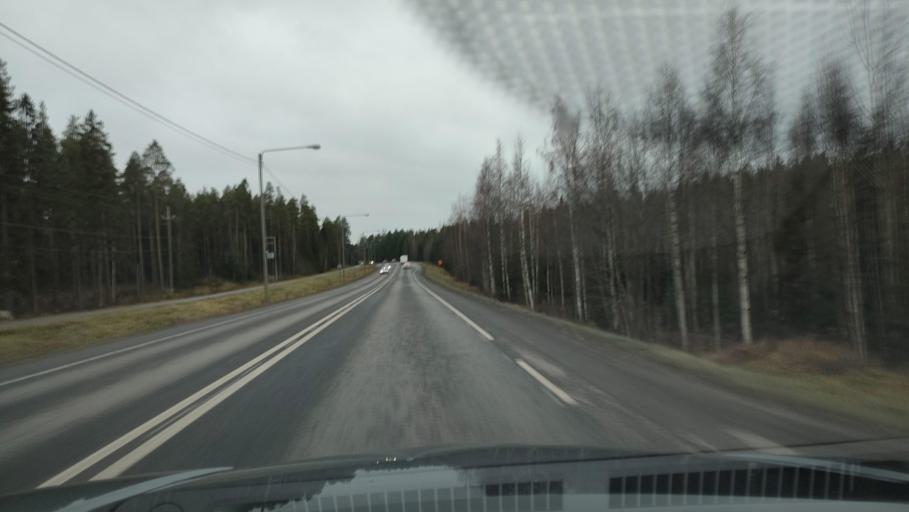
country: FI
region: Southern Ostrobothnia
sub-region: Seinaejoki
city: Ilmajoki
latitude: 62.7773
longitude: 22.6930
